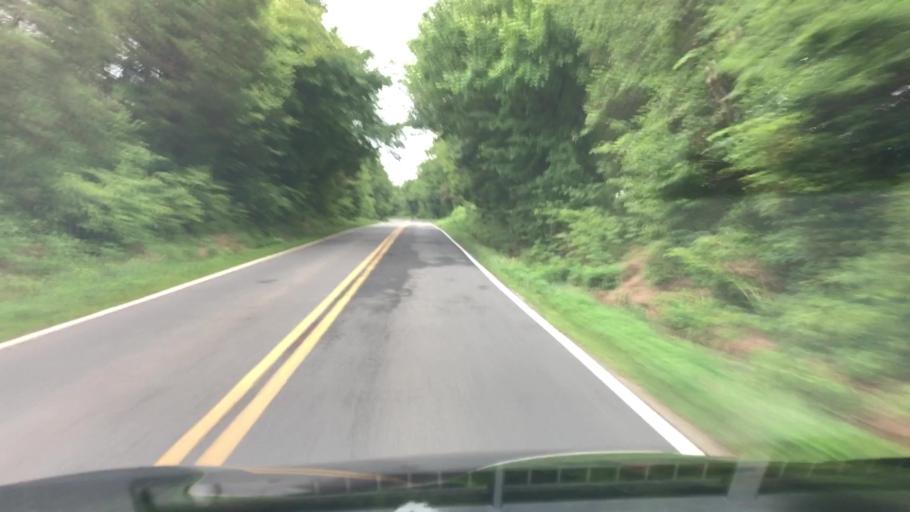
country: US
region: Virginia
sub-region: Prince William County
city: Nokesville
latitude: 38.6093
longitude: -77.6063
